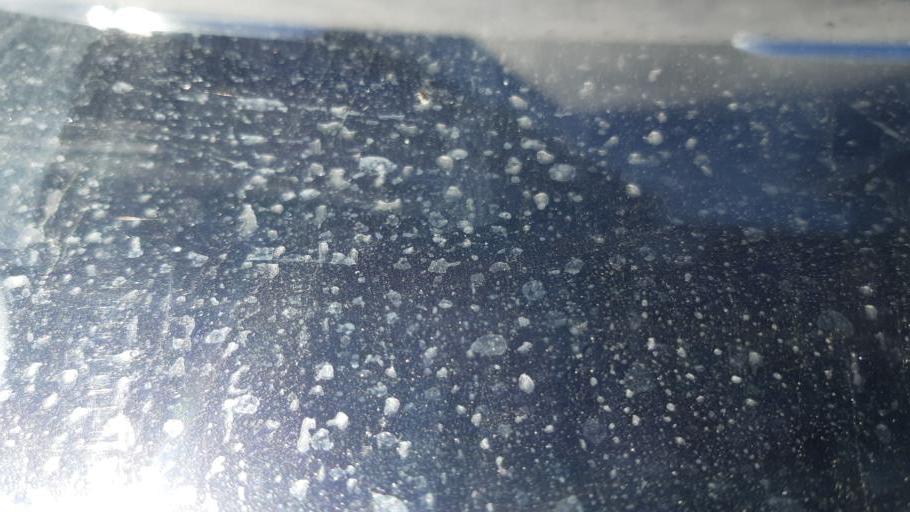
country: PT
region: Aveiro
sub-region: Agueda
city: Aguada de Cima
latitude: 40.5679
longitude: -8.3575
